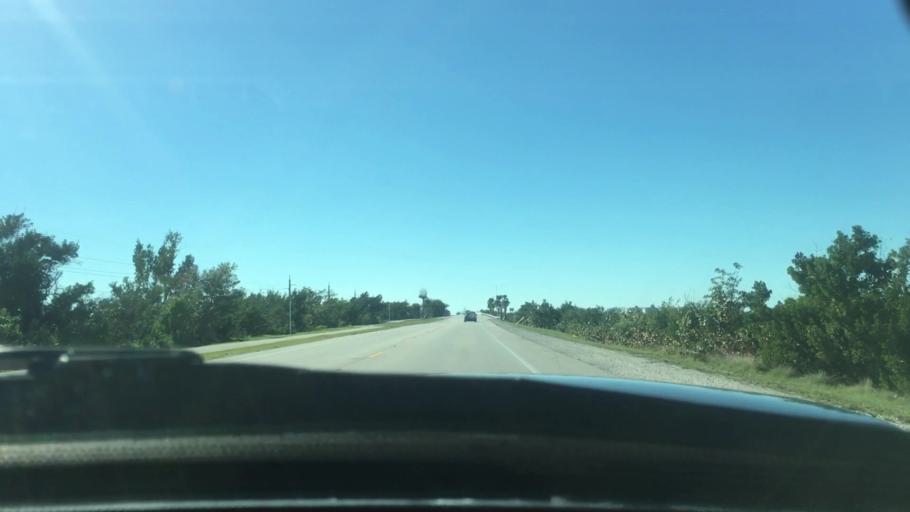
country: US
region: Florida
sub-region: Monroe County
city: Big Pine Key
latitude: 24.6682
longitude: -81.3803
